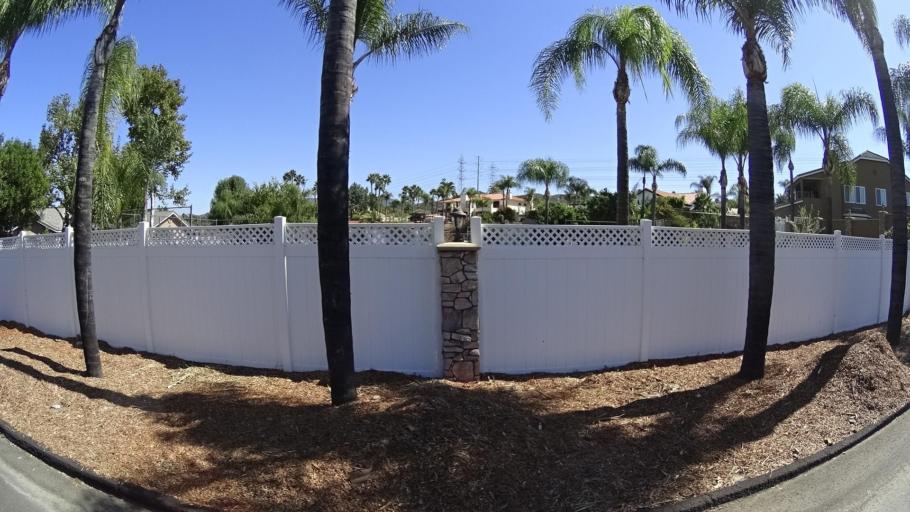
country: US
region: California
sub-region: San Diego County
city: Rancho San Diego
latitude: 32.7377
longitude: -116.9181
